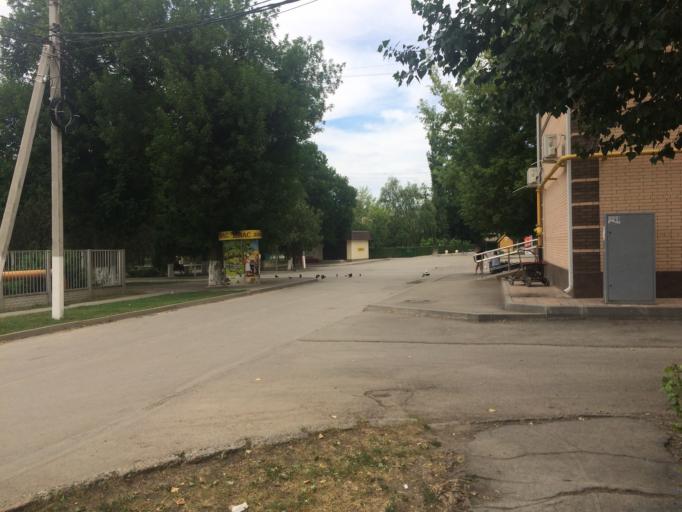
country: RU
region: Rostov
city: Sal'sk
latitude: 46.4765
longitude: 41.5391
